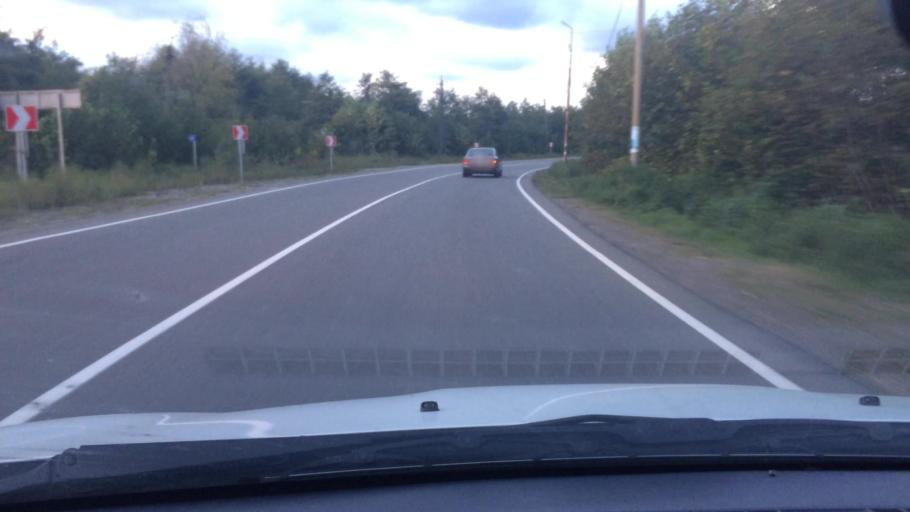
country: GE
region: Guria
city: Urek'i
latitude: 41.9670
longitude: 41.7737
